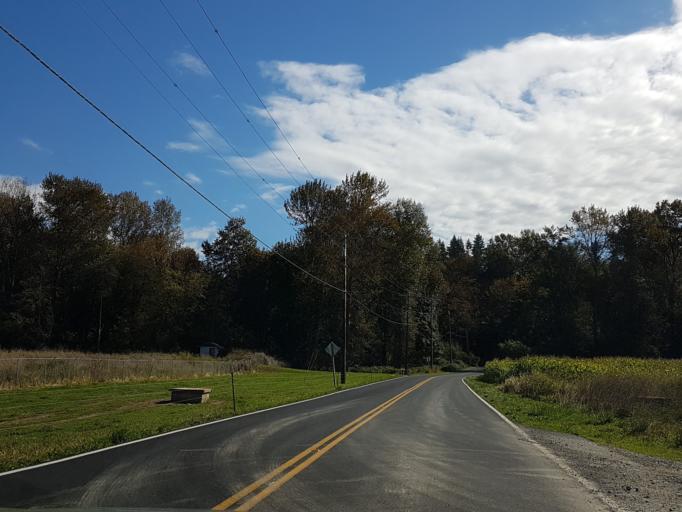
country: US
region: Washington
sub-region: Snohomish County
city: Monroe
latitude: 47.8132
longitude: -121.9855
